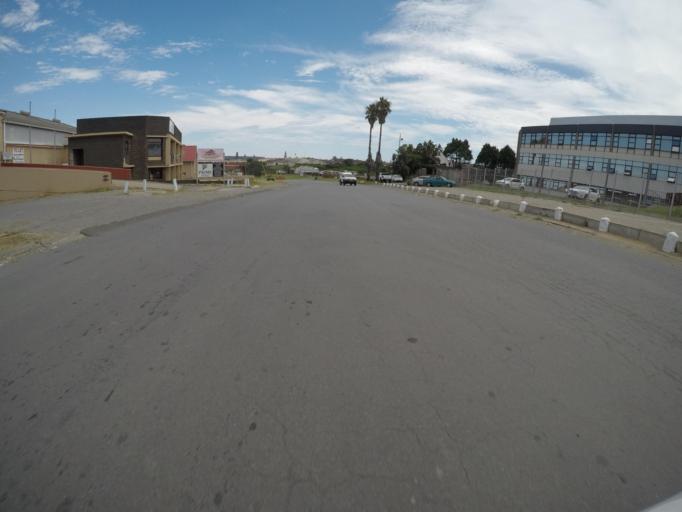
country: ZA
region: Eastern Cape
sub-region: Buffalo City Metropolitan Municipality
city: East London
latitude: -33.0321
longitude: 27.8798
